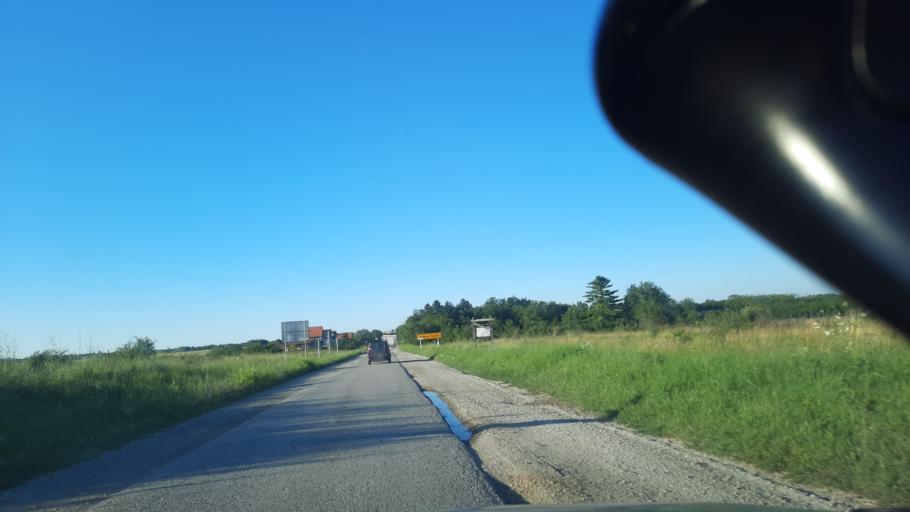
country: RS
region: Autonomna Pokrajina Vojvodina
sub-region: Sremski Okrug
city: Irig
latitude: 45.1093
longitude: 19.9313
